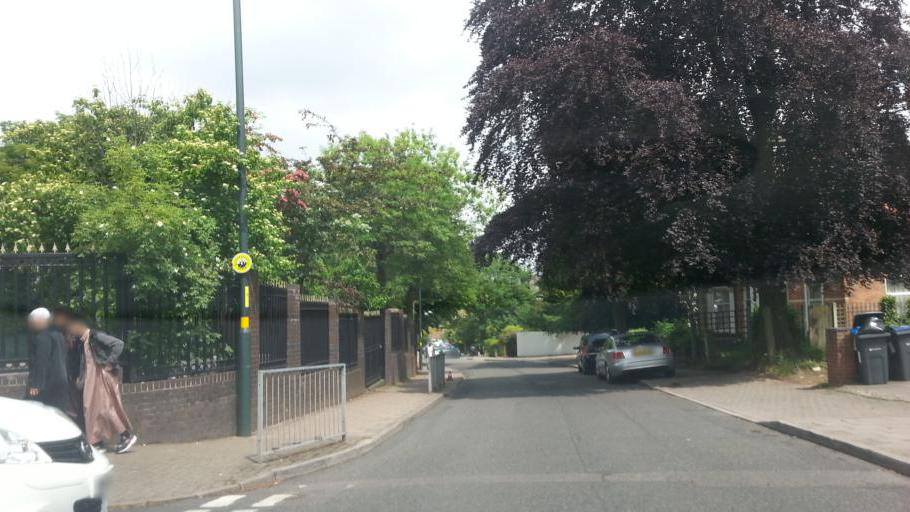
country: GB
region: England
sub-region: City and Borough of Birmingham
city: Birmingham
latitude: 52.4487
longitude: -1.8824
